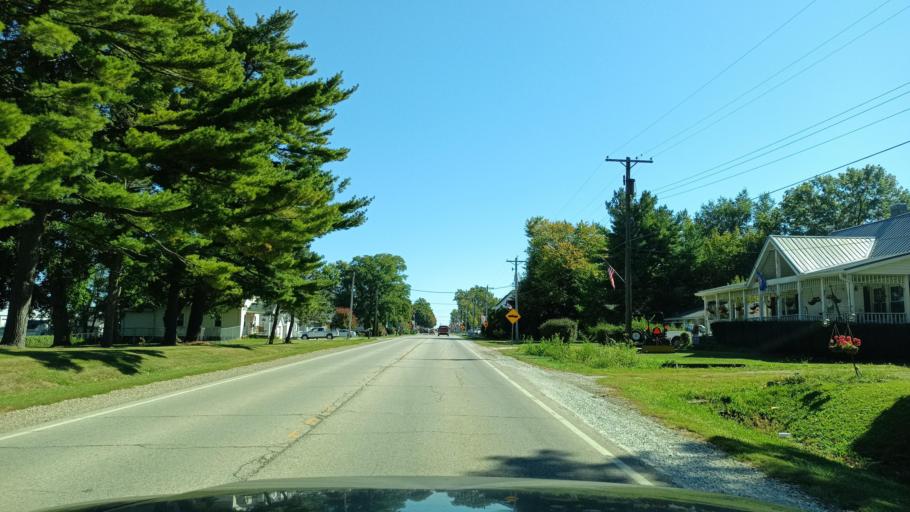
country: US
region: Illinois
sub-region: Peoria County
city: Dunlap
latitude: 40.7899
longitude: -89.7549
